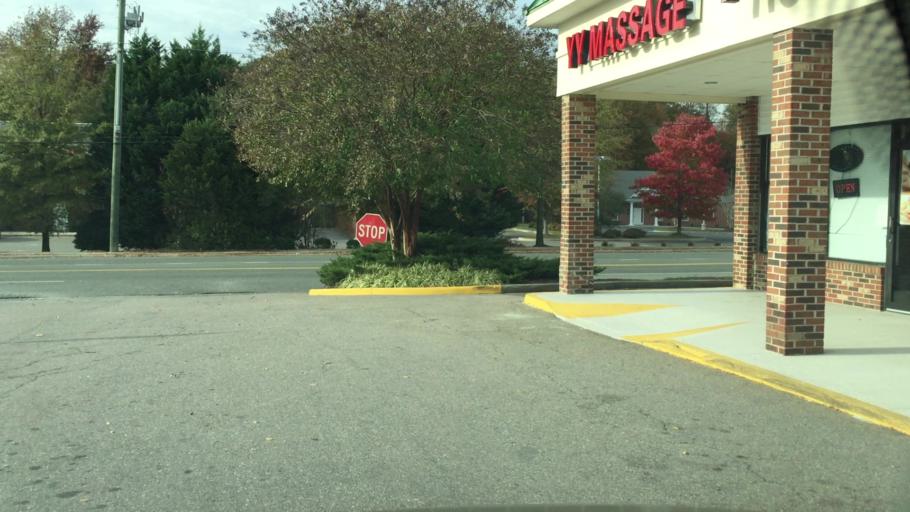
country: US
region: Virginia
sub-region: Chesterfield County
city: Bon Air
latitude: 37.5080
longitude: -77.5809
